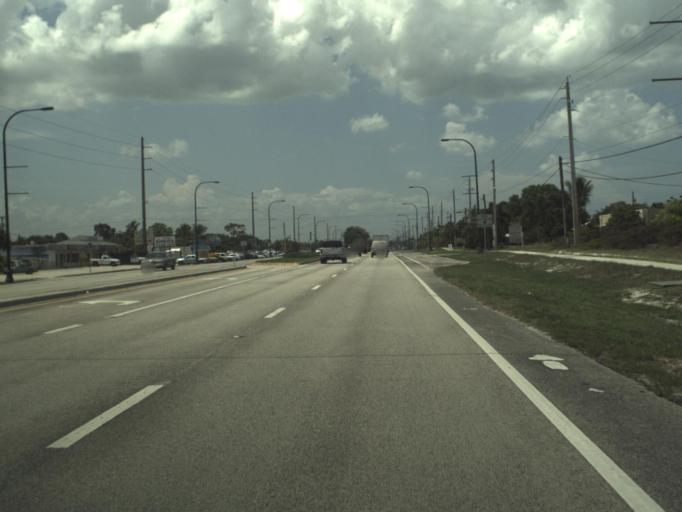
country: US
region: Florida
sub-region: Martin County
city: Hobe Sound
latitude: 27.0666
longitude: -80.1396
